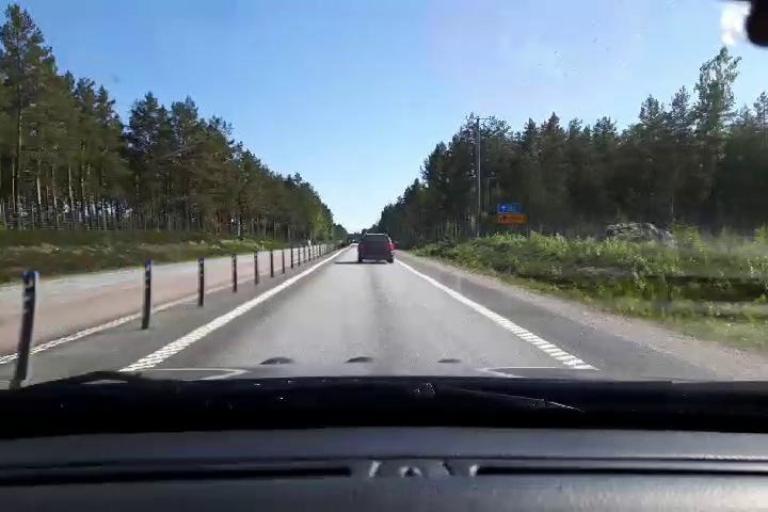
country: SE
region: Gaevleborg
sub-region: Gavle Kommun
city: Norrsundet
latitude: 61.0271
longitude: 16.9754
